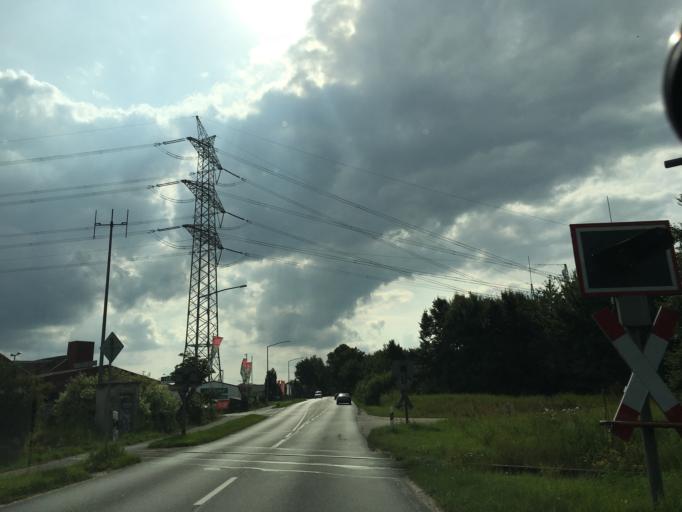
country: DE
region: Lower Saxony
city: Melbeck
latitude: 53.2194
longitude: 10.3816
